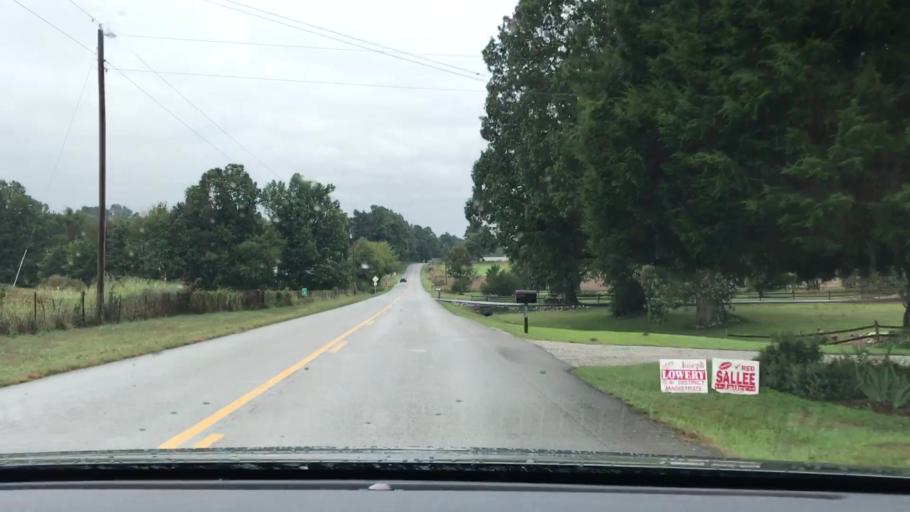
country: US
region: Kentucky
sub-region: McLean County
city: Calhoun
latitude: 37.4840
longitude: -87.2475
